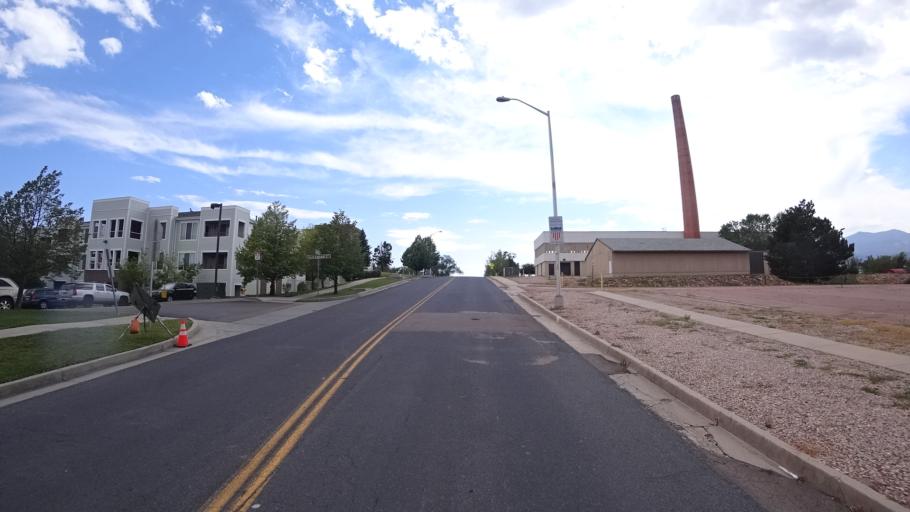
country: US
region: Colorado
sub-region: El Paso County
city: Colorado Springs
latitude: 38.8329
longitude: -104.8082
